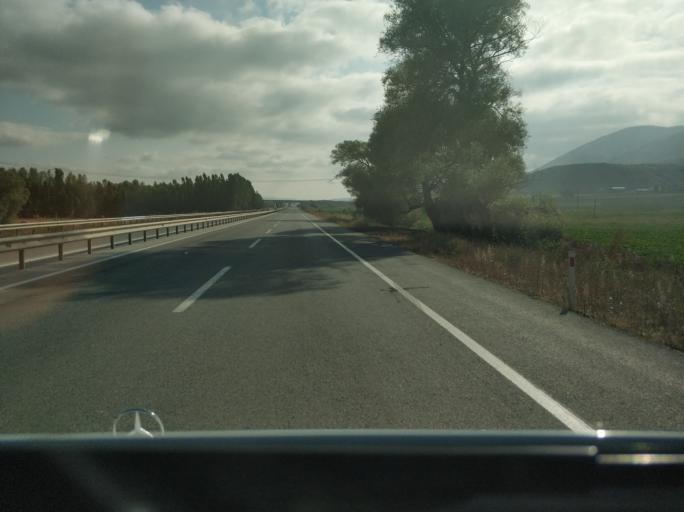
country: TR
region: Sivas
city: Yildizeli
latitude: 39.8519
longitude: 36.5349
